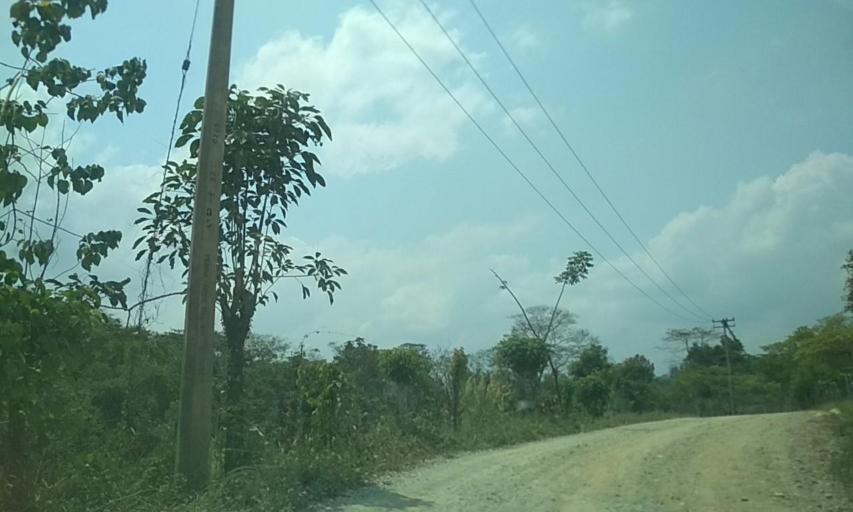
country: MX
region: Tabasco
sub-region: Huimanguillo
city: Francisco Rueda
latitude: 17.6403
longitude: -93.8241
